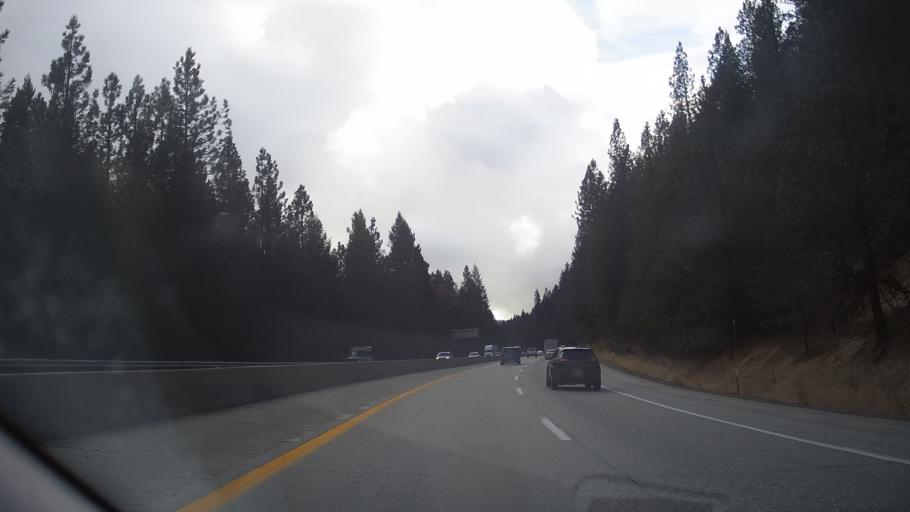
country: US
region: California
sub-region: Placer County
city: Foresthill
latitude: 39.2228
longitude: -120.7686
